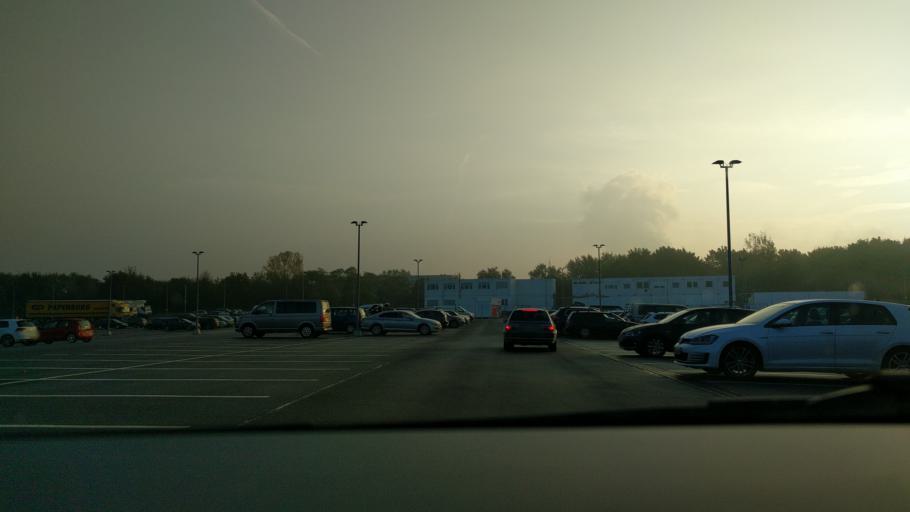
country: DE
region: Lower Saxony
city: Tappenbeck
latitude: 52.4434
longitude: 10.7372
